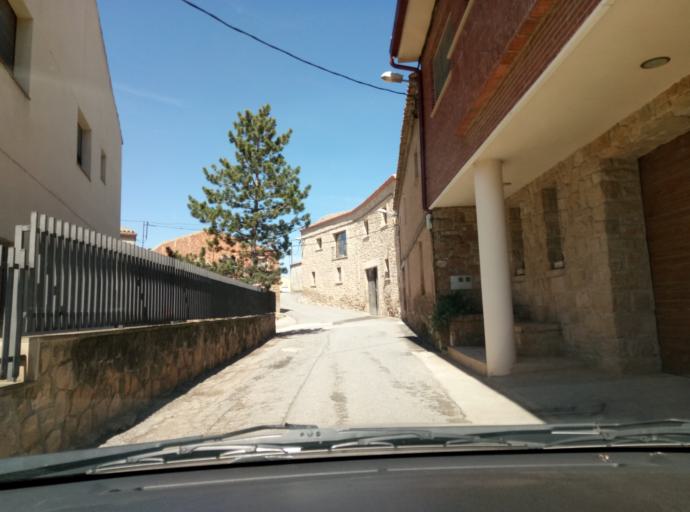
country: ES
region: Catalonia
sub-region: Provincia de Lleida
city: Vinaixa
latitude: 41.4230
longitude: 0.9346
